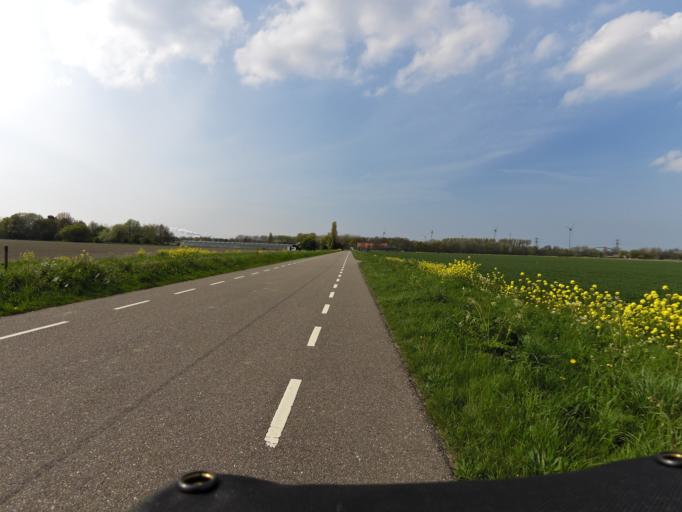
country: NL
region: South Holland
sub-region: Gemeente Brielle
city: Brielle
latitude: 51.9203
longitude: 4.1405
